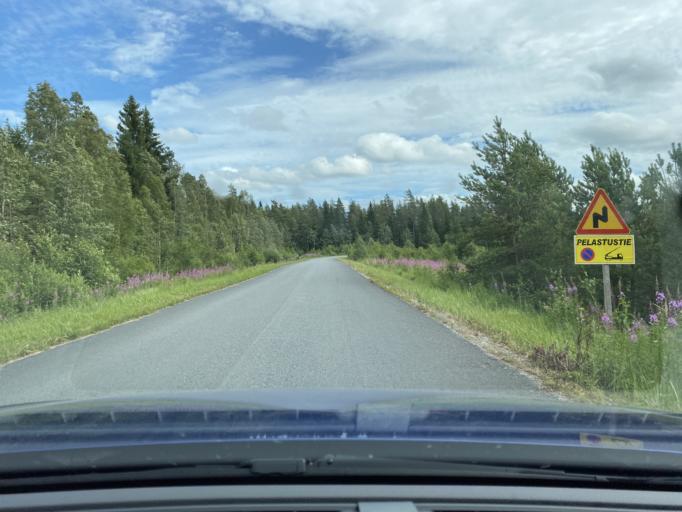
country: FI
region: Southern Ostrobothnia
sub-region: Seinaejoki
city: Jurva
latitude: 62.6266
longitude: 22.0246
